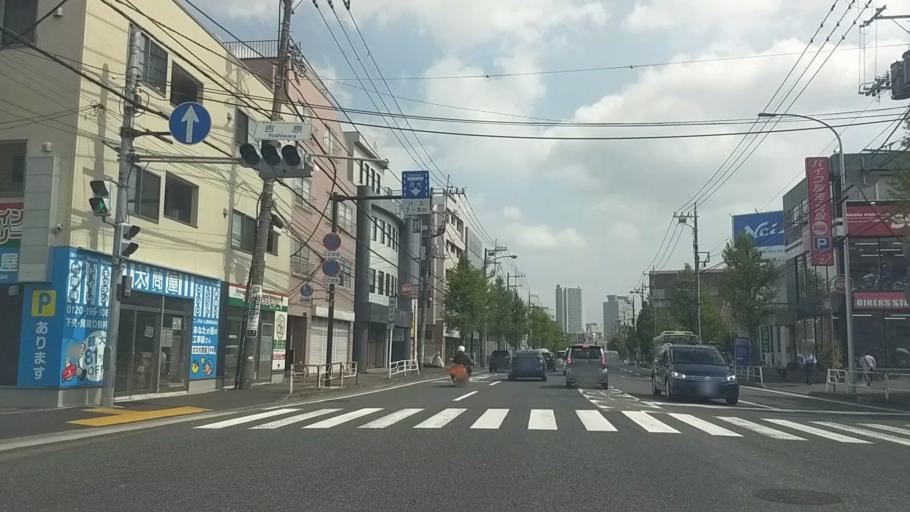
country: JP
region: Kanagawa
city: Yokohama
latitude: 35.3979
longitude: 139.5873
